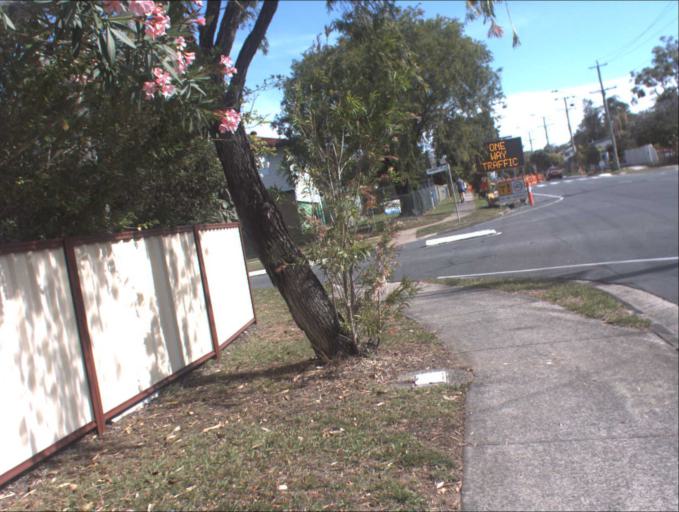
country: AU
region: Queensland
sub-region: Logan
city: Woodridge
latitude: -27.6233
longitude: 153.1106
